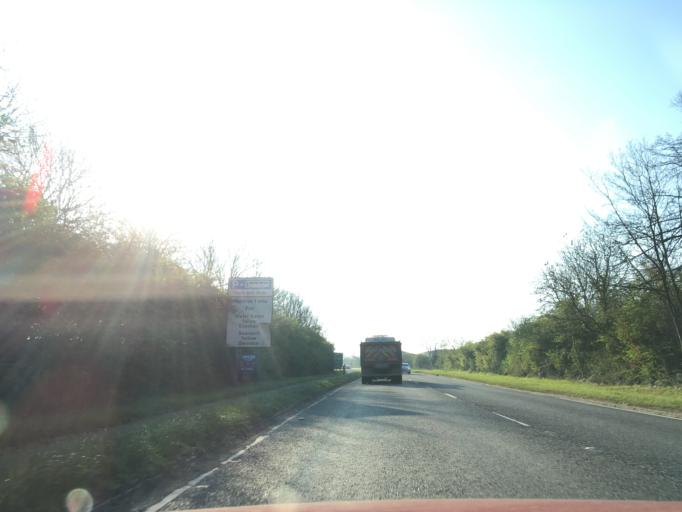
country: GB
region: England
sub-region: Oxfordshire
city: Yarnton
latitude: 51.7897
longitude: -1.2874
